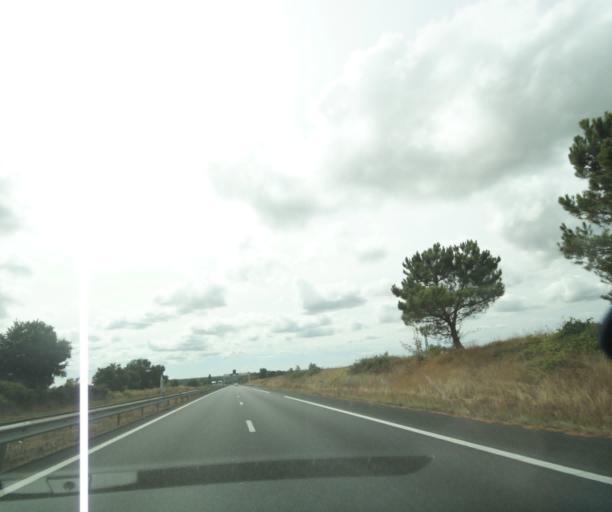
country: FR
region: Aquitaine
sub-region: Departement de la Gironde
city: Marcillac
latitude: 45.2816
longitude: -0.5509
